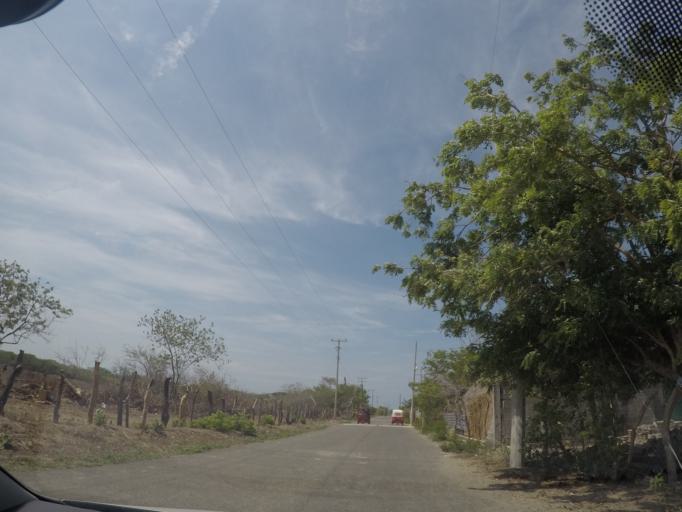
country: MX
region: Oaxaca
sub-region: Salina Cruz
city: Salina Cruz
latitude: 16.2000
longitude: -95.1196
